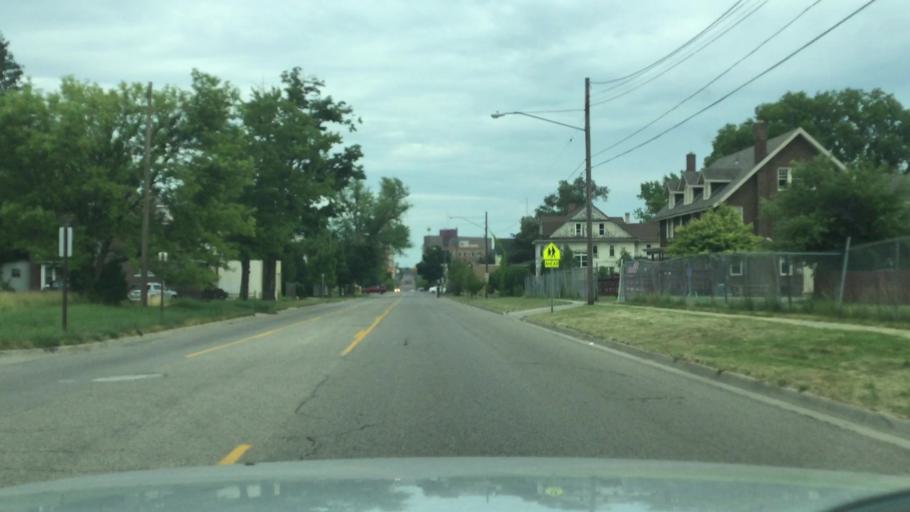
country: US
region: Michigan
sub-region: Genesee County
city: Flint
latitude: 43.0245
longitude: -83.6981
